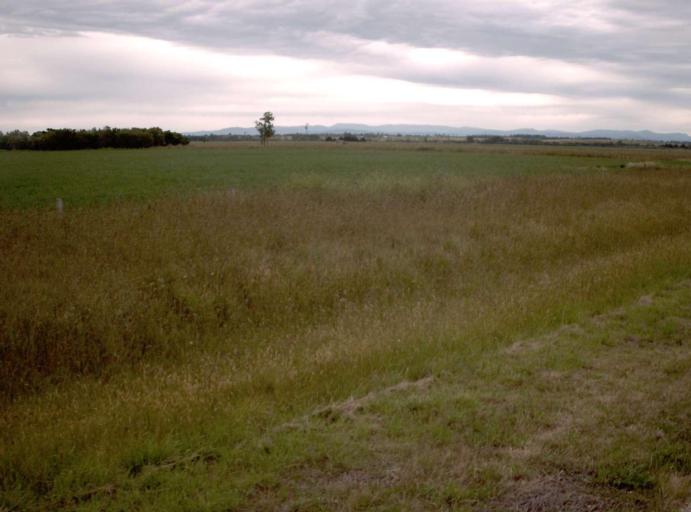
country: AU
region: Victoria
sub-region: Wellington
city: Sale
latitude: -38.0444
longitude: 147.1755
